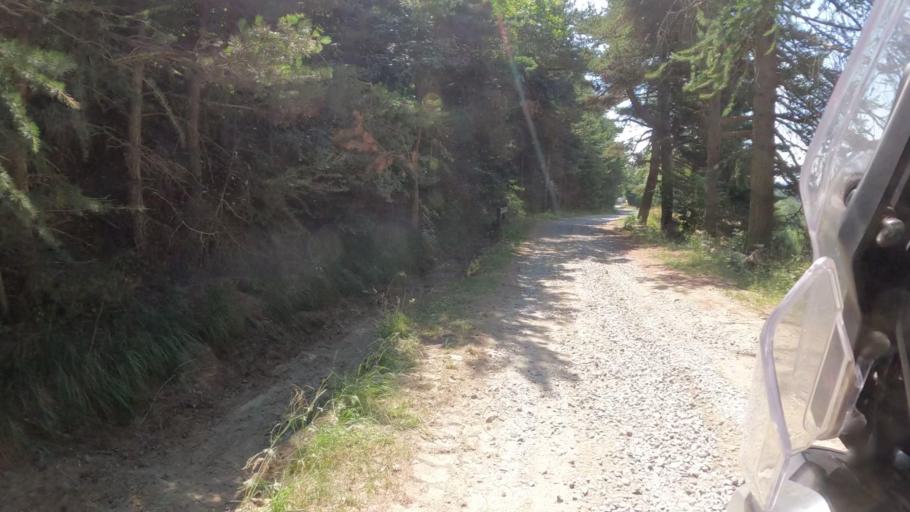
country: IT
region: Piedmont
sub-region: Provincia di Torino
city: Borgone Susa
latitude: 45.1585
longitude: 7.2622
